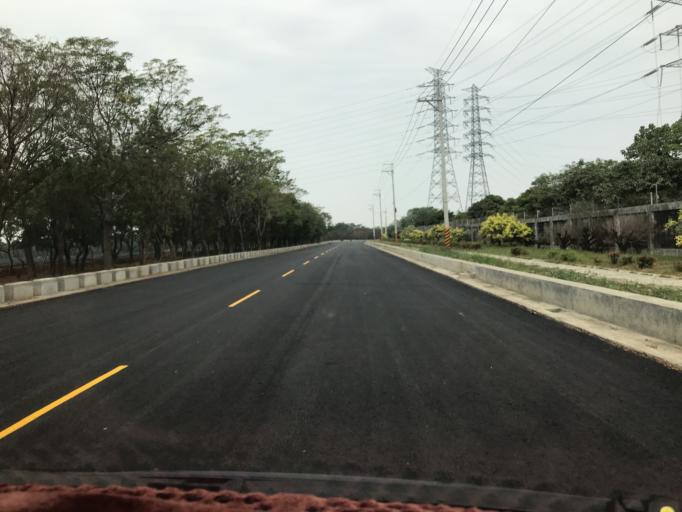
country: TW
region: Taiwan
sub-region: Pingtung
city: Pingtung
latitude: 22.4178
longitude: 120.6073
